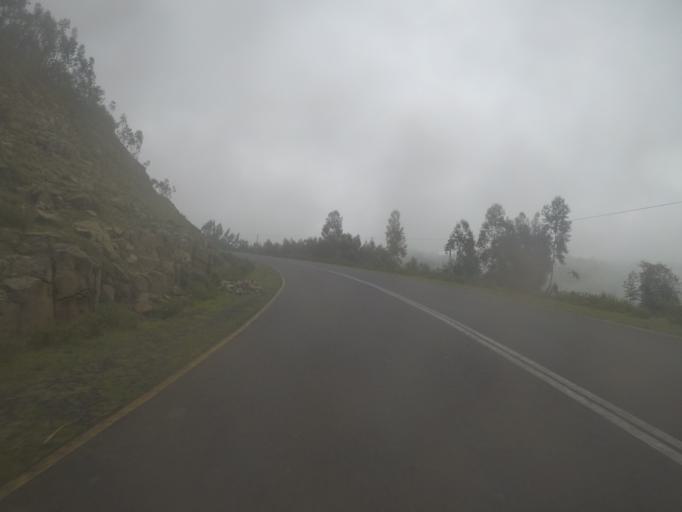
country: ET
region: Amhara
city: Gondar
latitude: 12.7486
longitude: 37.5302
